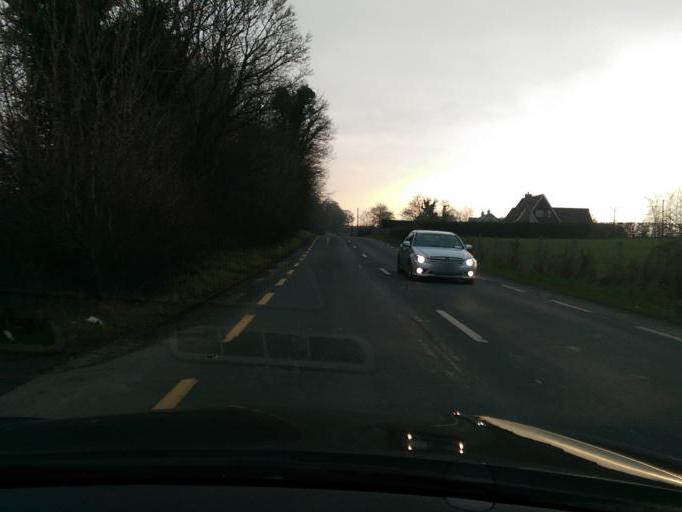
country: IE
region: Leinster
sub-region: An Longfort
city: Ballymahon
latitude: 53.5046
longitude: -7.8375
